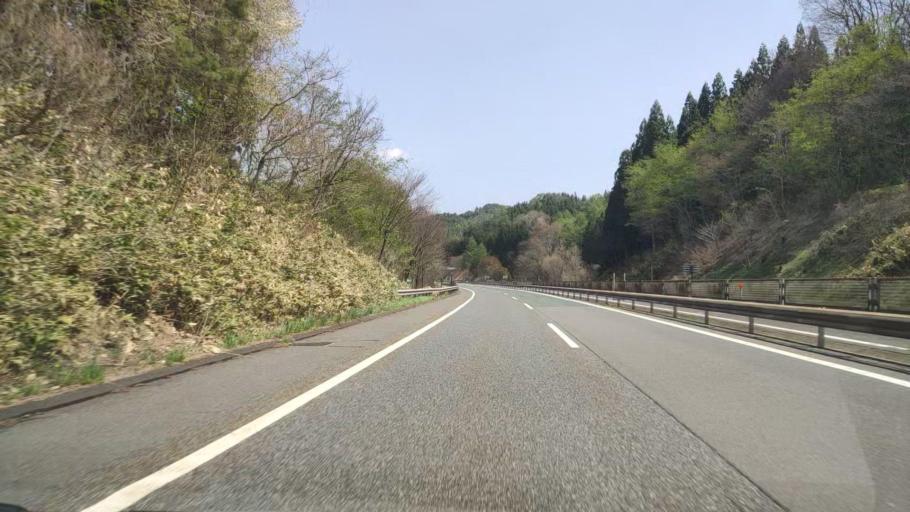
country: JP
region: Iwate
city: Ichinohe
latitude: 40.1841
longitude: 141.1694
